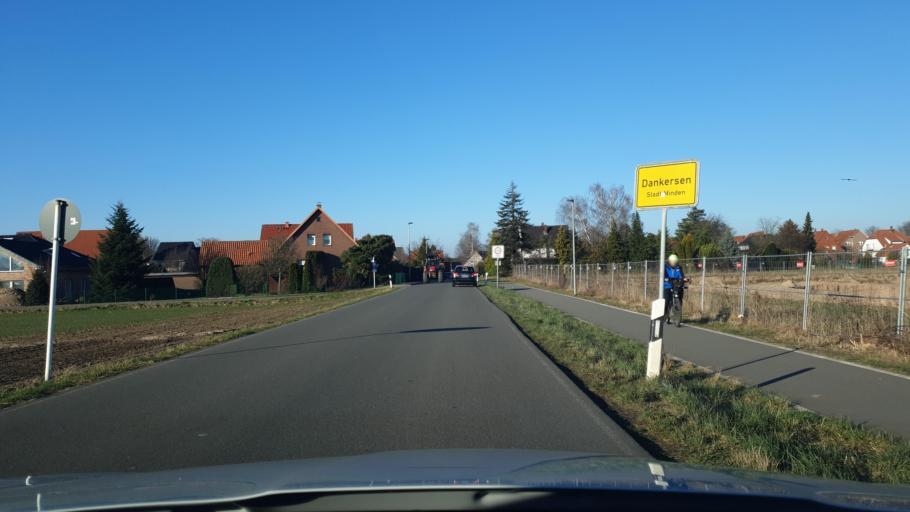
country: DE
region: North Rhine-Westphalia
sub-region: Regierungsbezirk Detmold
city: Minden
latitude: 52.2860
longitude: 8.9641
